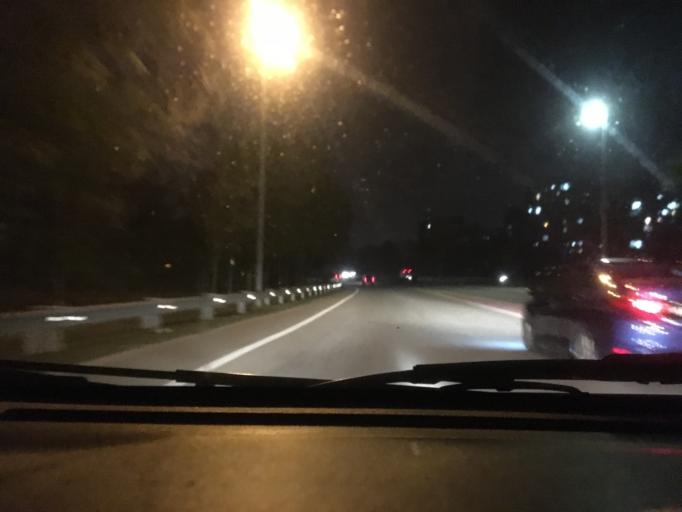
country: MY
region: Putrajaya
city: Putrajaya
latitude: 2.9136
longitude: 101.6623
